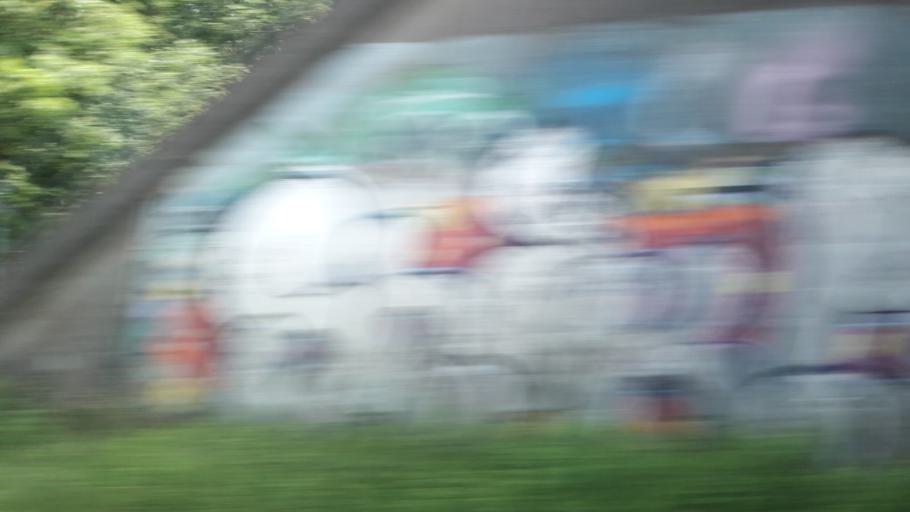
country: DE
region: North Rhine-Westphalia
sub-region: Regierungsbezirk Detmold
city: Verl
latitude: 51.9470
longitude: 8.5498
